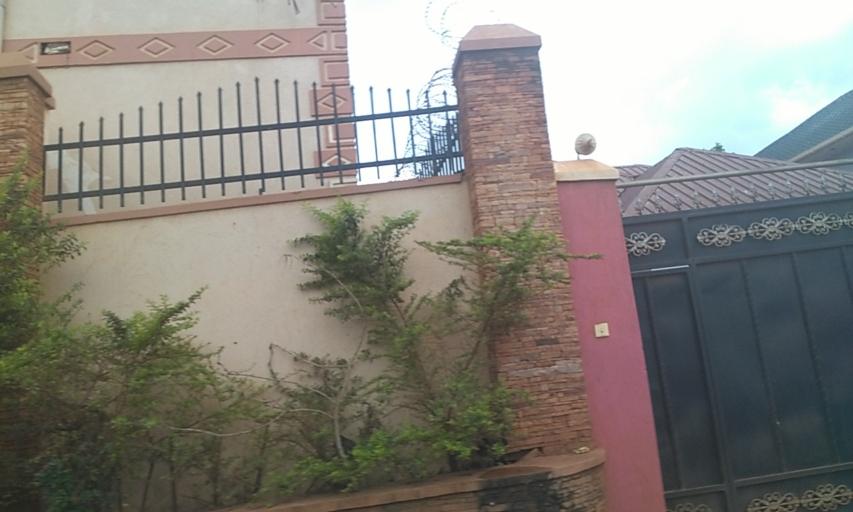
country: UG
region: Central Region
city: Kampala Central Division
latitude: 0.3526
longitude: 32.6056
